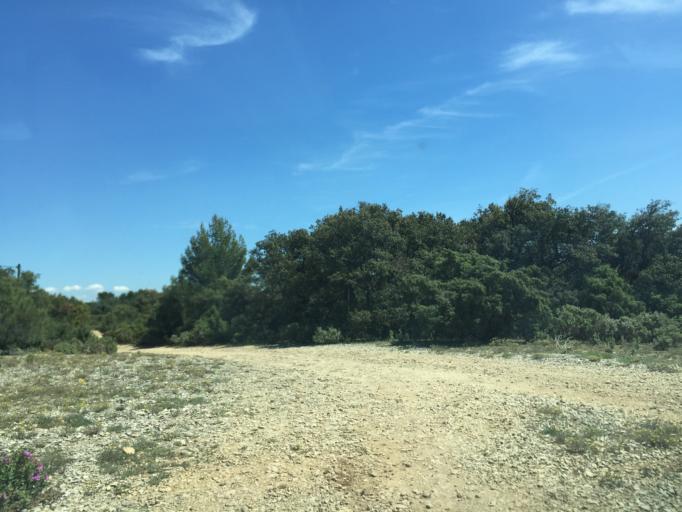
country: FR
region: Provence-Alpes-Cote d'Azur
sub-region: Departement du Vaucluse
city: Chateauneuf-du-Pape
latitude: 44.0523
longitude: 4.8062
